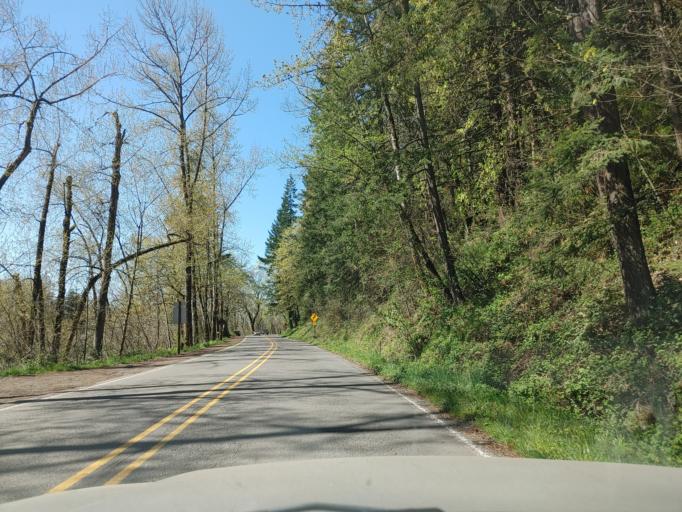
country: US
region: Oregon
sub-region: Multnomah County
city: Troutdale
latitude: 45.5389
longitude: -122.3761
